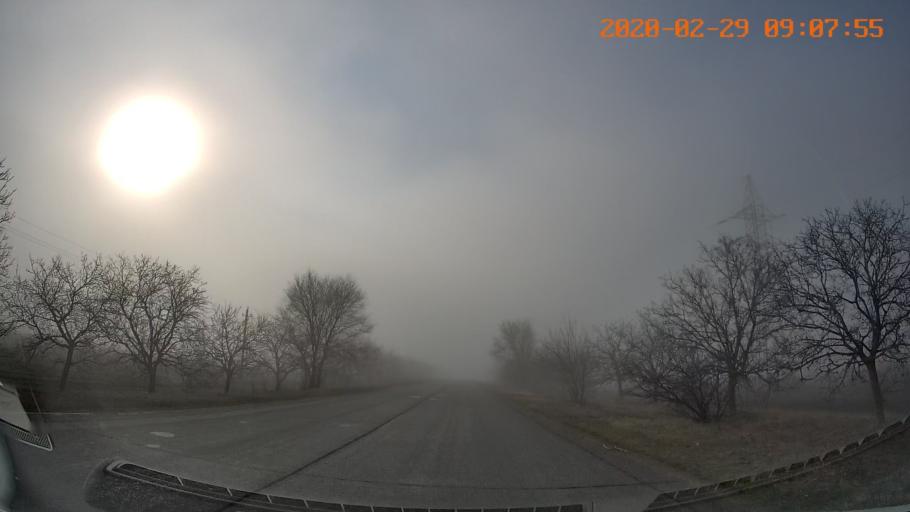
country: MD
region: Telenesti
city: Tiraspolul Nou
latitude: 46.8567
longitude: 29.7506
